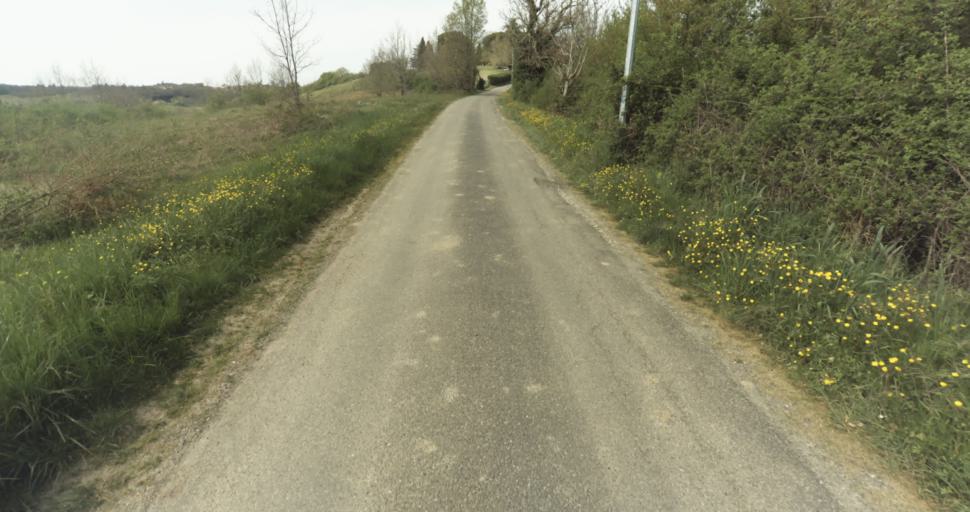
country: FR
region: Midi-Pyrenees
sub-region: Departement du Tarn-et-Garonne
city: Moissac
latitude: 44.1277
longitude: 1.1113
